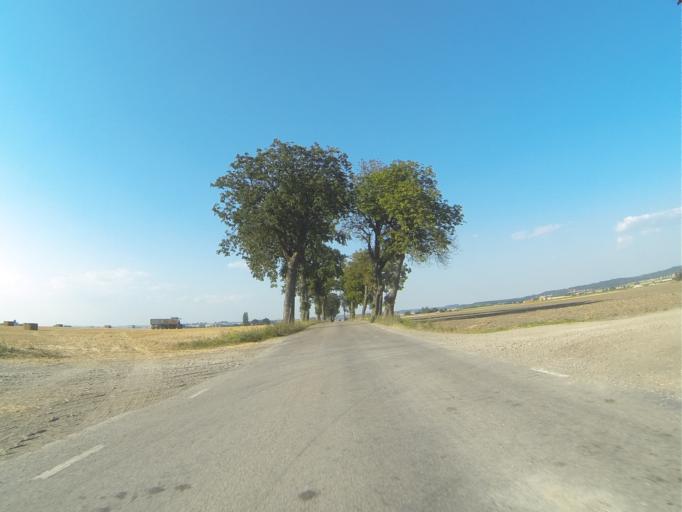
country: SE
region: Skane
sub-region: Lunds Kommun
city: Genarp
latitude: 55.6031
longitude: 13.3656
